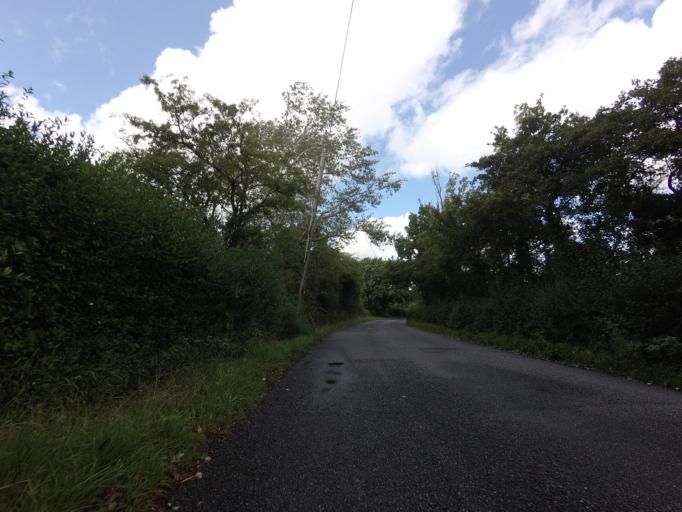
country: GB
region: England
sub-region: Kent
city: Hadlow
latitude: 51.2325
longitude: 0.3321
